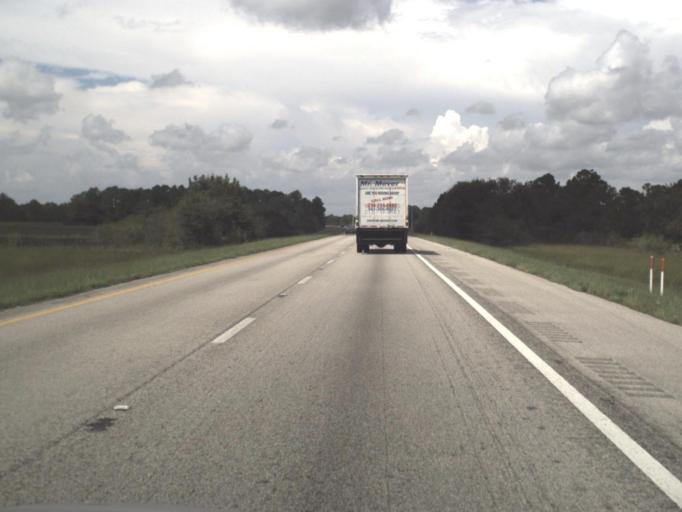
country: US
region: Florida
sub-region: Lee County
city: Suncoast Estates
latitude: 26.7922
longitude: -81.9055
